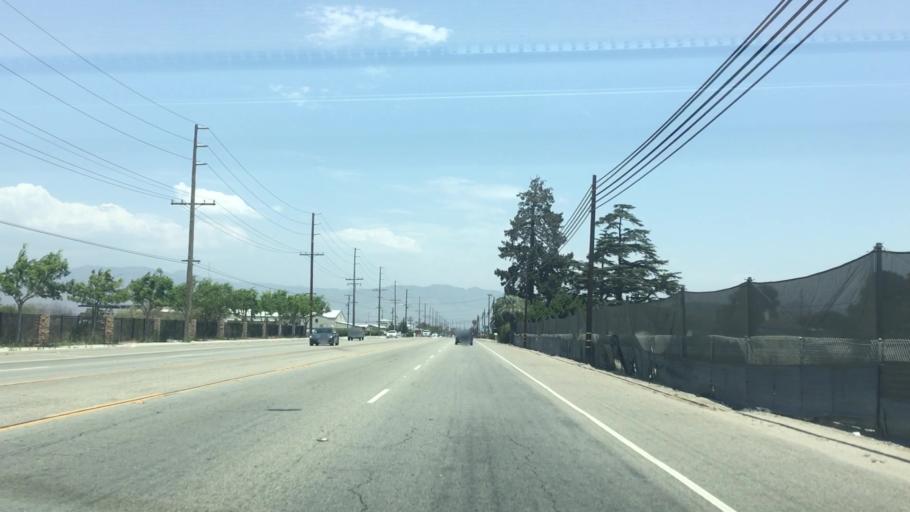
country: US
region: California
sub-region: Ventura County
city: El Rio
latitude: 34.2469
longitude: -119.1618
